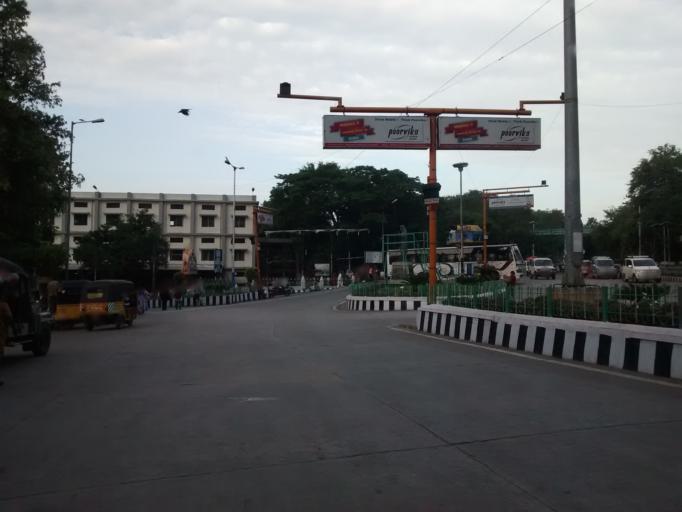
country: IN
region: Andhra Pradesh
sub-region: Chittoor
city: Akkarampalle
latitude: 13.6468
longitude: 79.4060
